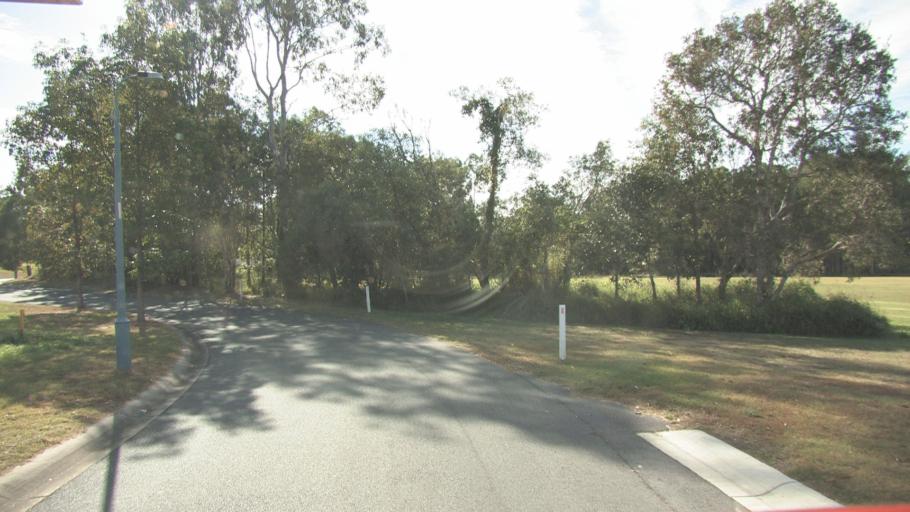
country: AU
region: Queensland
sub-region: Brisbane
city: Forest Lake
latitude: -27.6561
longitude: 152.9896
